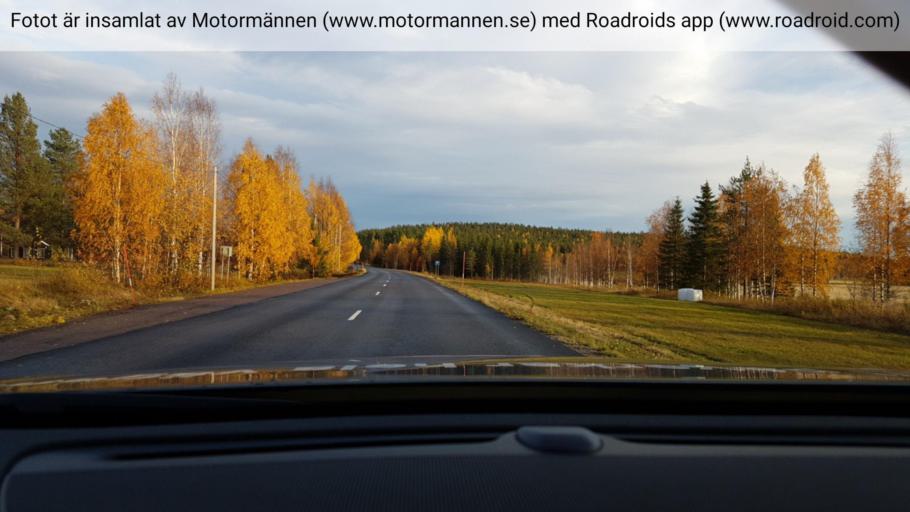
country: SE
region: Norrbotten
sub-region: Overkalix Kommun
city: OEverkalix
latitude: 66.9694
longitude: 22.6500
